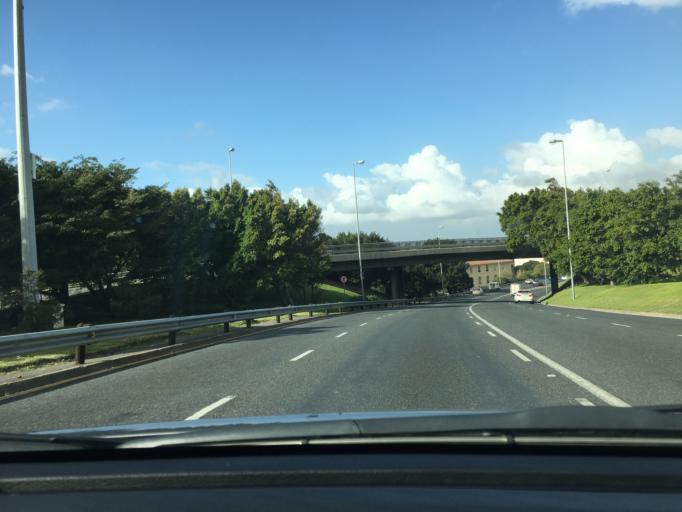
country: ZA
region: Western Cape
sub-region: City of Cape Town
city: Rosebank
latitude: -33.9431
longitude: 18.4633
